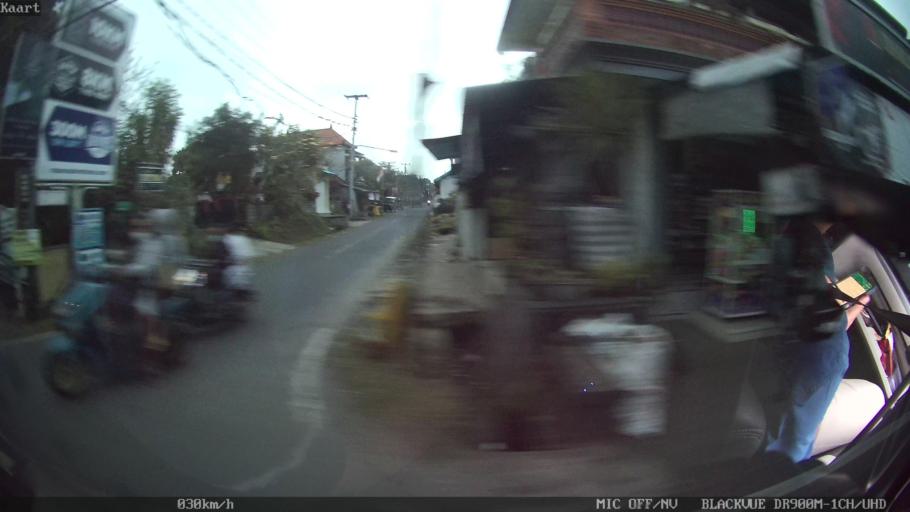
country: ID
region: Bali
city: Badung
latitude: -8.4365
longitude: 115.2446
